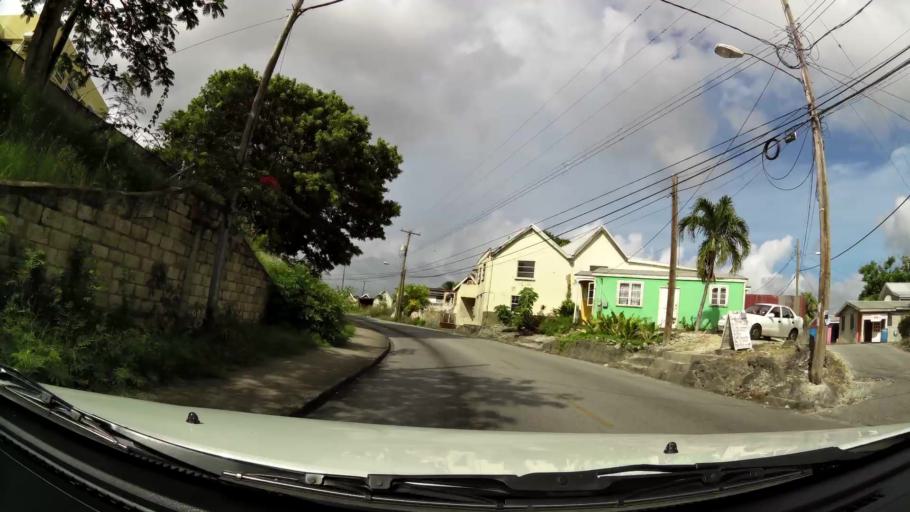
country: BB
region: Saint Michael
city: Bridgetown
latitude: 13.1117
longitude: -59.6027
